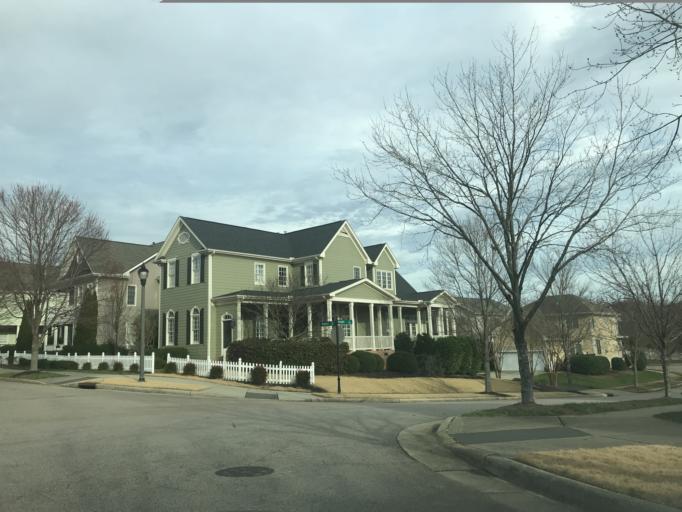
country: US
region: North Carolina
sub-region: Wake County
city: Wake Forest
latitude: 35.9252
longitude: -78.5727
